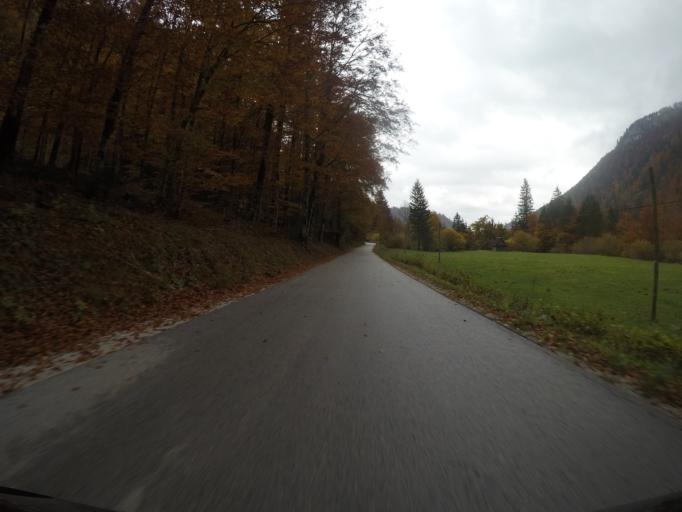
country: SI
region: Jesenice
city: Hrusica
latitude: 46.3950
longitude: 14.0088
